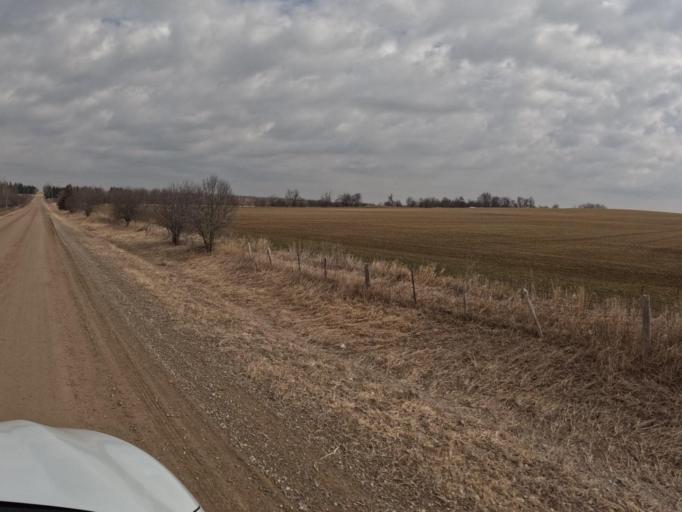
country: CA
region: Ontario
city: Orangeville
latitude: 43.9321
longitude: -80.1883
